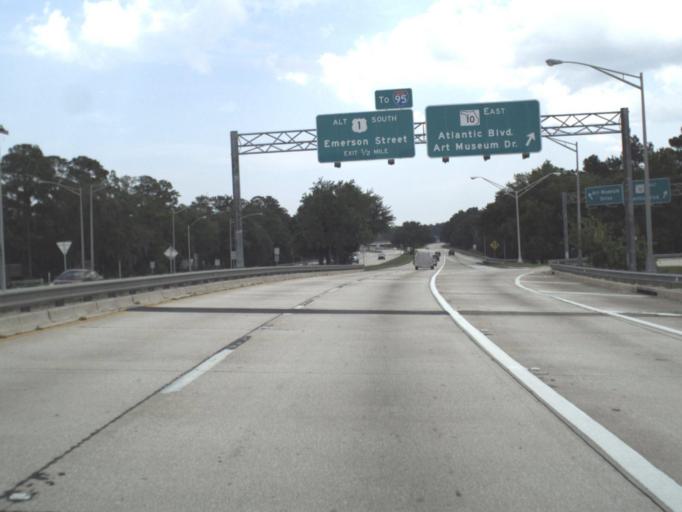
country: US
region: Florida
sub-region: Duval County
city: Jacksonville
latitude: 30.3079
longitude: -81.6189
